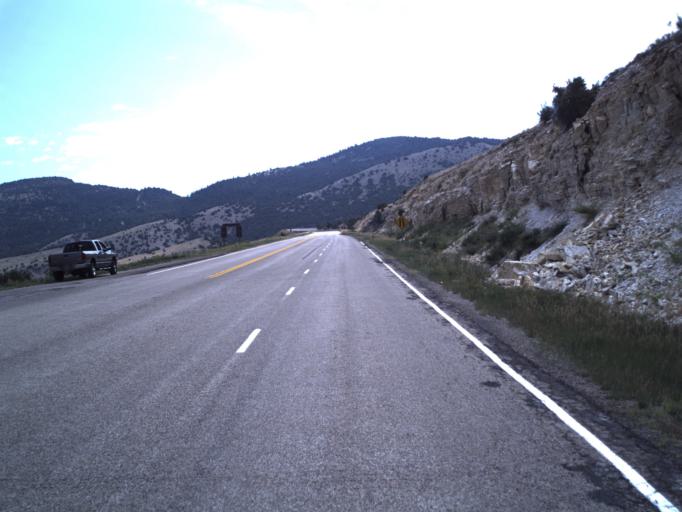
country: US
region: Utah
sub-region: Daggett County
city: Manila
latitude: 40.9158
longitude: -109.6847
